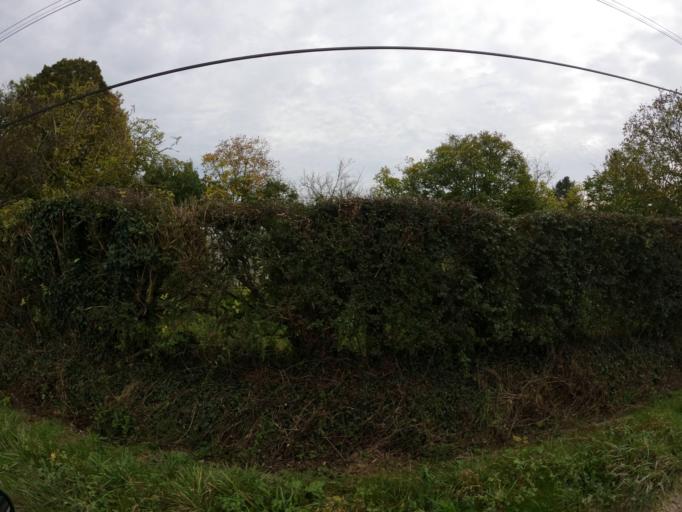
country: FR
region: Pays de la Loire
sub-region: Departement de Maine-et-Loire
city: Saint-Christophe-du-Bois
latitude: 47.0233
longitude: -0.9752
